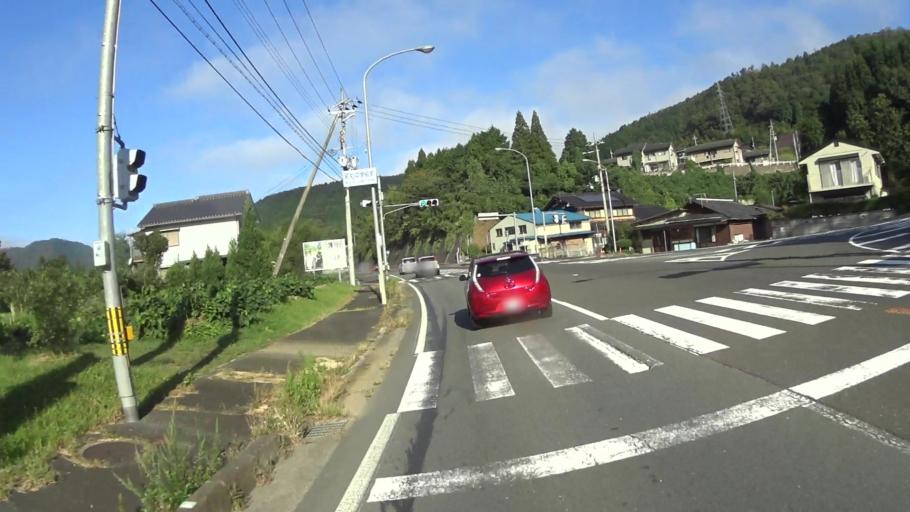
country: JP
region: Kyoto
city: Ayabe
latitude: 35.2592
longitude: 135.4104
